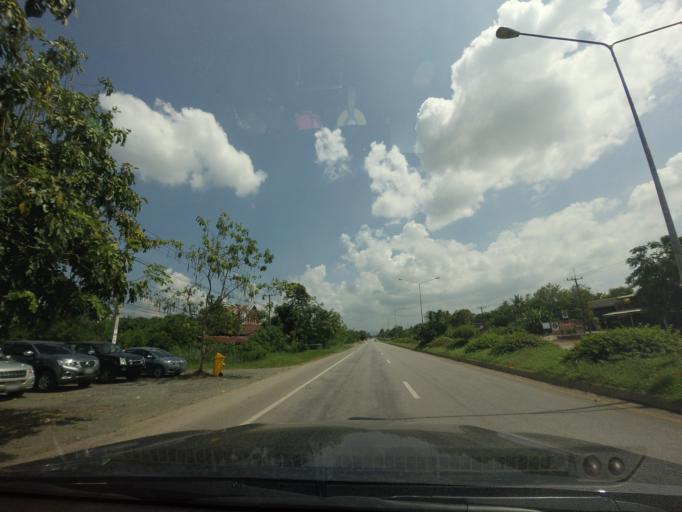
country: TH
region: Phetchabun
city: Phetchabun
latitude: 16.2584
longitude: 101.0568
